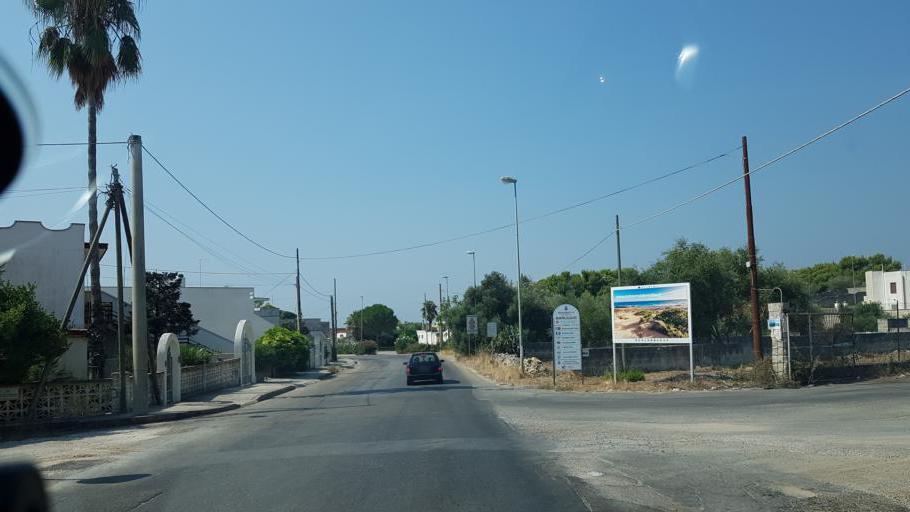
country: IT
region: Apulia
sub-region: Provincia di Taranto
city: Maruggio
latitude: 40.3299
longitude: 17.5749
